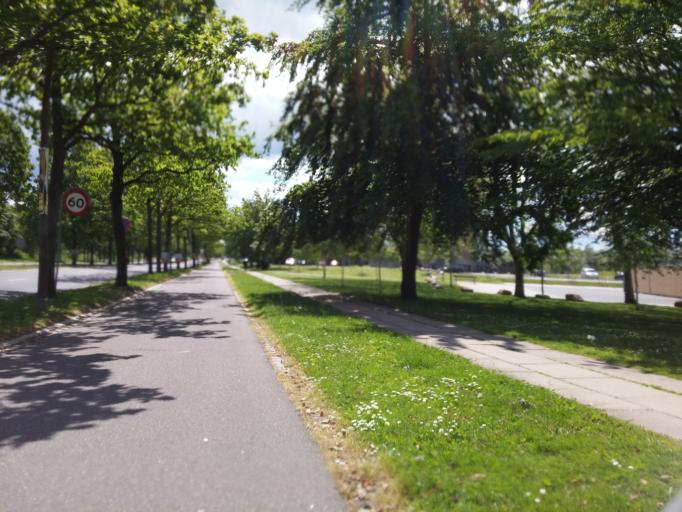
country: DK
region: South Denmark
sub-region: Odense Kommune
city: Seden
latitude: 55.4154
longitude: 10.4385
